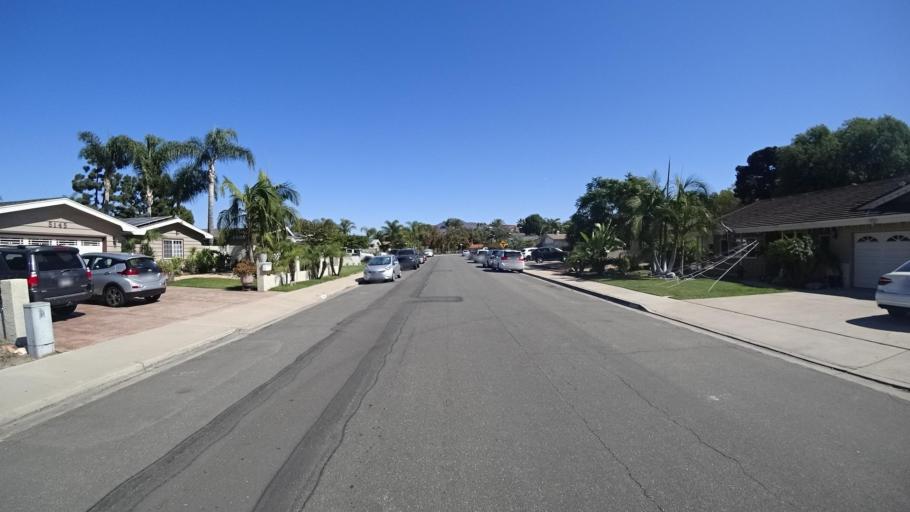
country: US
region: California
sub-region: San Diego County
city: Bonita
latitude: 32.6682
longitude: -117.0186
